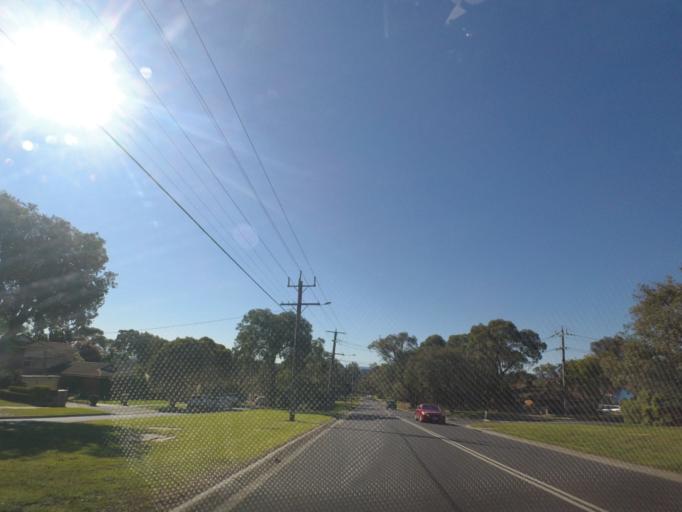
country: AU
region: Victoria
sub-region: Maroondah
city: Croydon Hills
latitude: -37.7766
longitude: 145.2751
